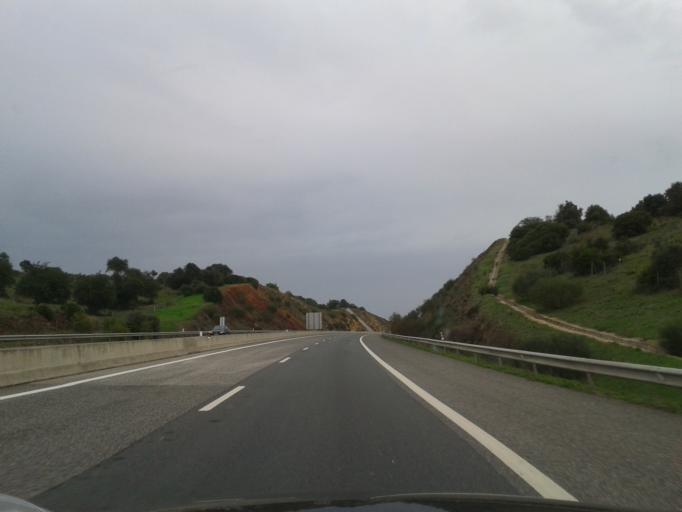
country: PT
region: Faro
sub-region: Portimao
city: Portimao
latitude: 37.1725
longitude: -8.5189
